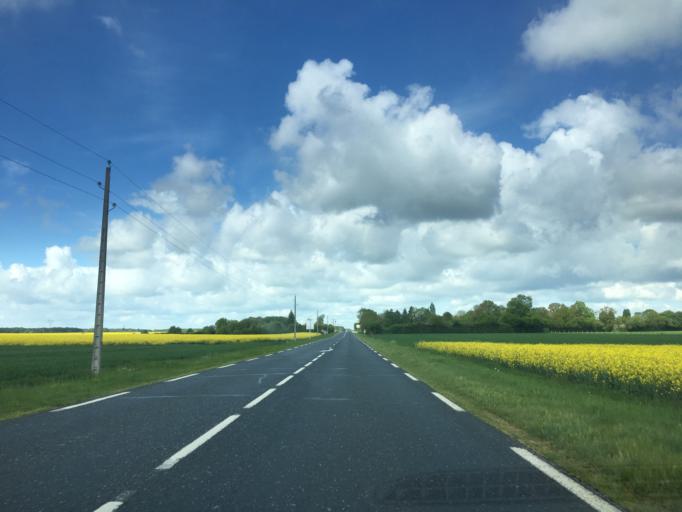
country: FR
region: Haute-Normandie
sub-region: Departement de l'Eure
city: Bourth
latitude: 48.7463
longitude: 0.8161
